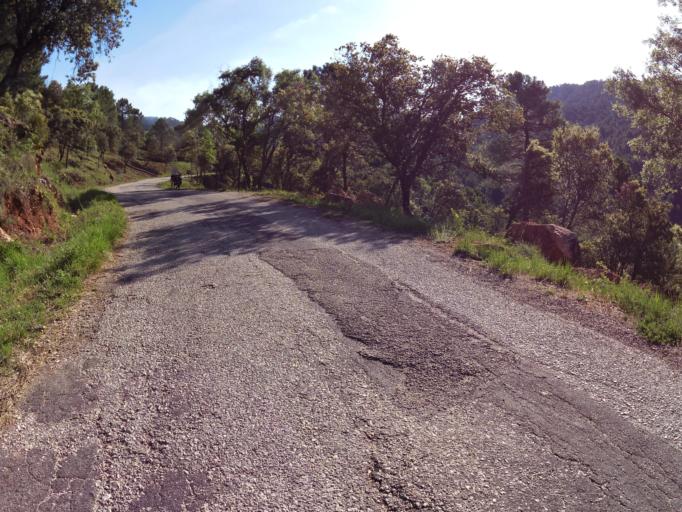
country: ES
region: Castille-La Mancha
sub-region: Provincia de Albacete
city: Riopar
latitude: 38.5183
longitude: -2.4558
